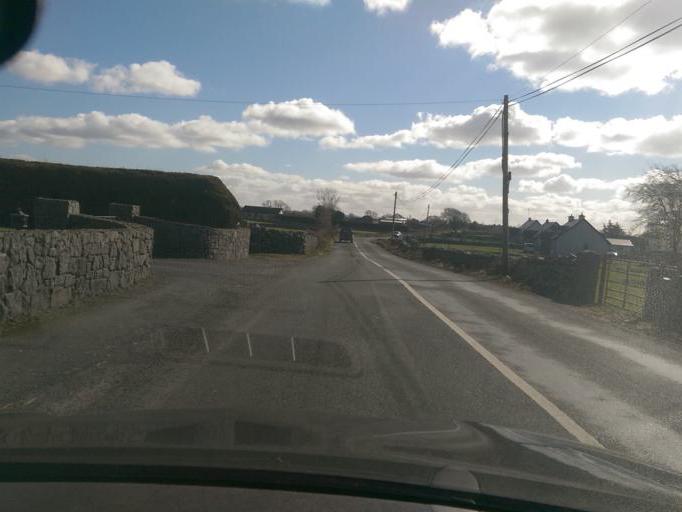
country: IE
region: Connaught
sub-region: County Galway
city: Athenry
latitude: 53.3253
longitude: -8.7645
